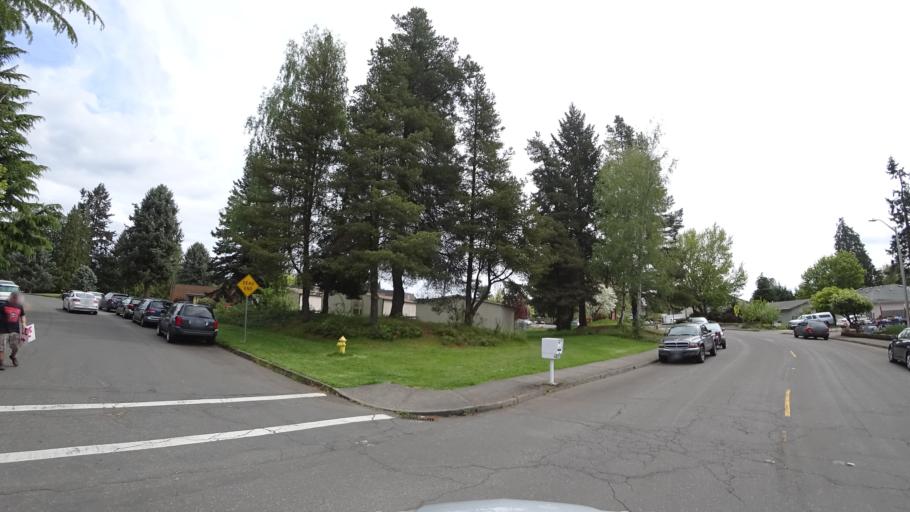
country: US
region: Oregon
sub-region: Washington County
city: Hillsboro
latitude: 45.5301
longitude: -122.9969
